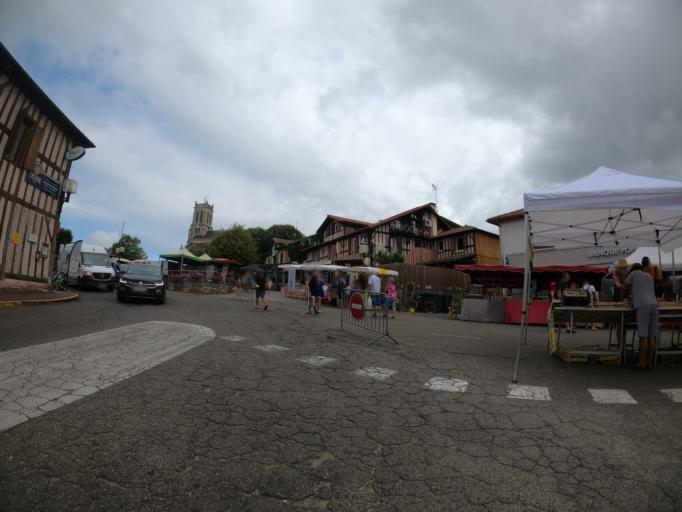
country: FR
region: Aquitaine
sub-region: Departement des Landes
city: Leon
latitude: 43.8750
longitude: -1.3022
